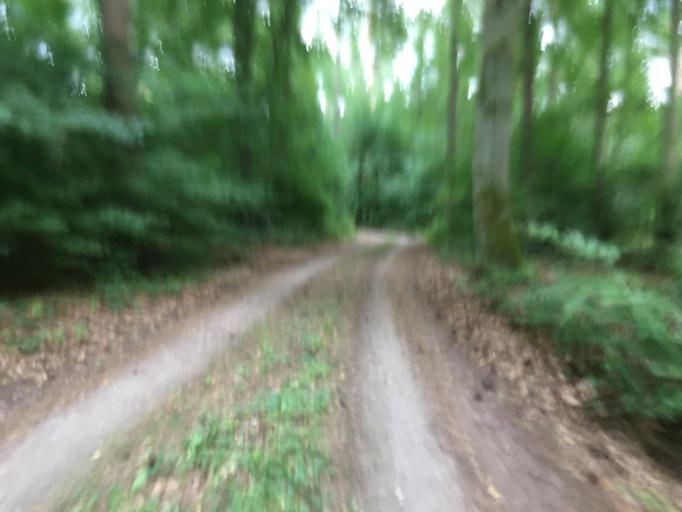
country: DE
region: Brandenburg
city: Lychen
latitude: 53.1206
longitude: 13.2480
